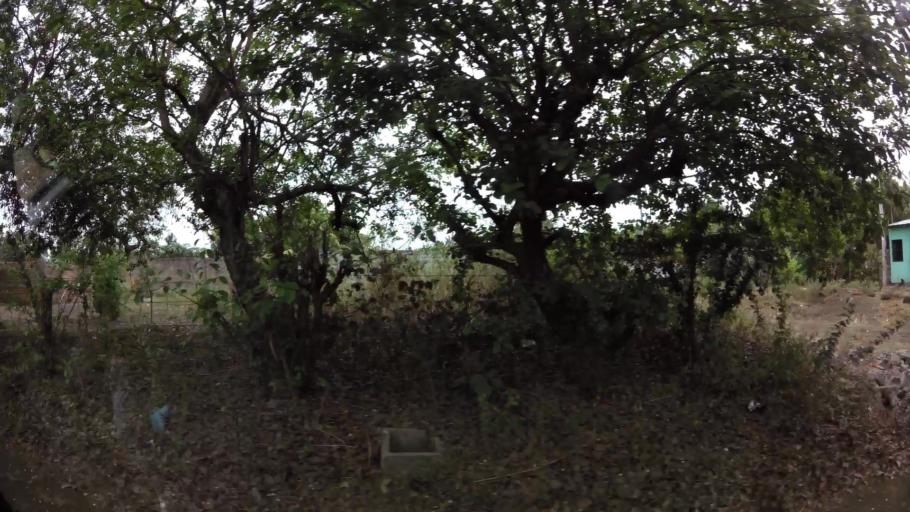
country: NI
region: Chinandega
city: Chinandega
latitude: 12.6242
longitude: -87.1131
